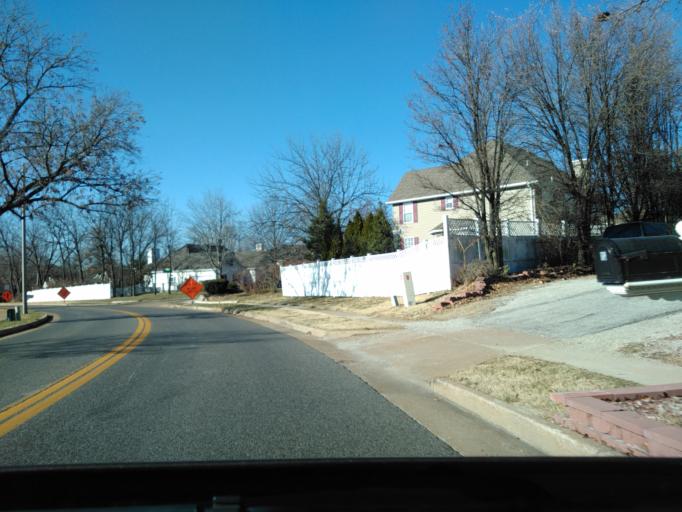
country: US
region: Missouri
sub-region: Saint Louis County
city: Ballwin
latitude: 38.5984
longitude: -90.5494
